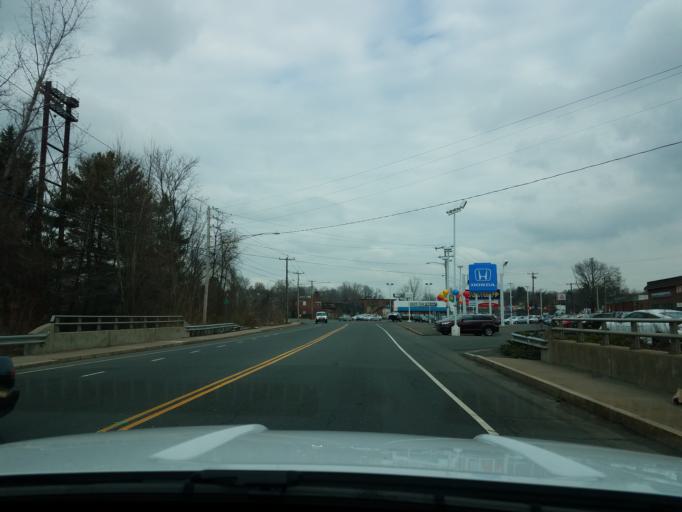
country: US
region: Connecticut
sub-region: Hartford County
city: Kensington
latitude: 41.6484
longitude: -72.7713
